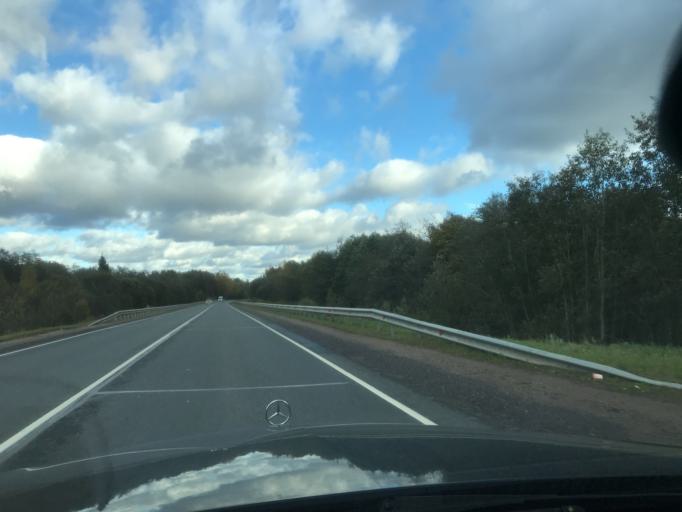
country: RU
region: Pskov
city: Novosokol'niki
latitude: 56.3504
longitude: 29.8601
